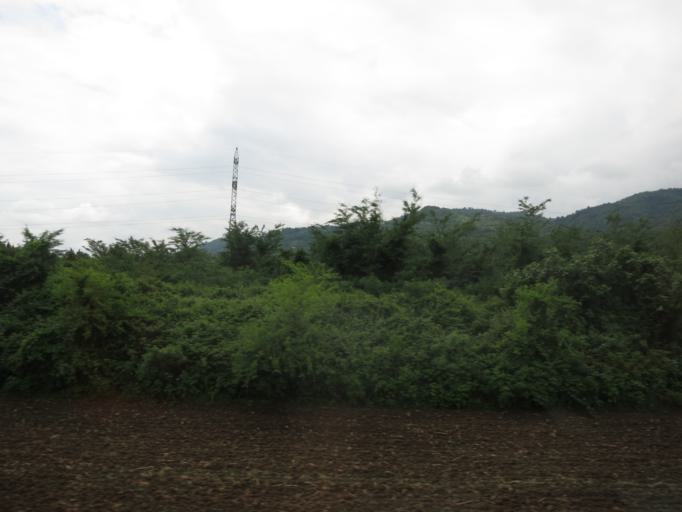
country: GE
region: Imereti
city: Samtredia
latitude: 42.1101
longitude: 42.3247
